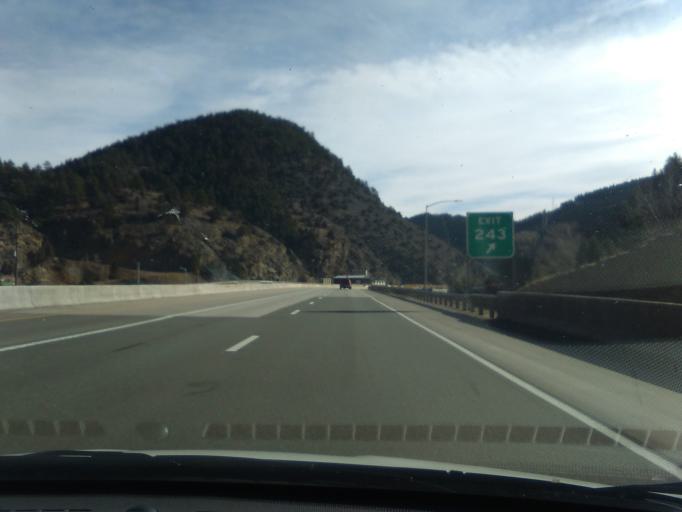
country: US
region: Colorado
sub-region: Clear Creek County
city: Idaho Springs
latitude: 39.7466
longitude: -105.4629
